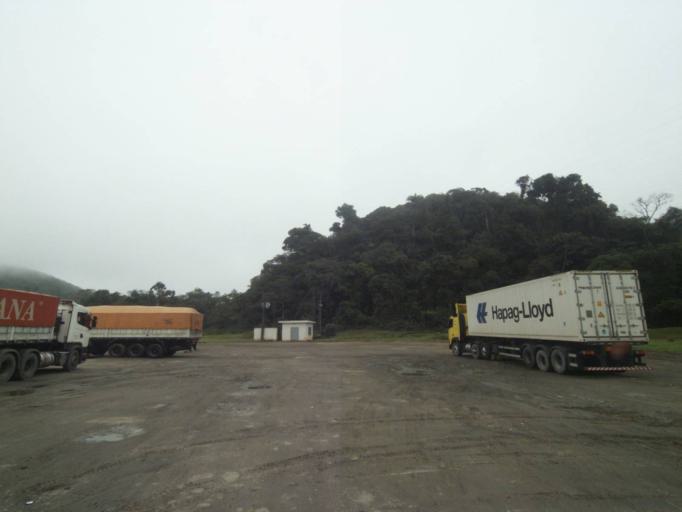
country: BR
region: Parana
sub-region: Paranagua
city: Paranagua
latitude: -25.5614
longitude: -48.5916
